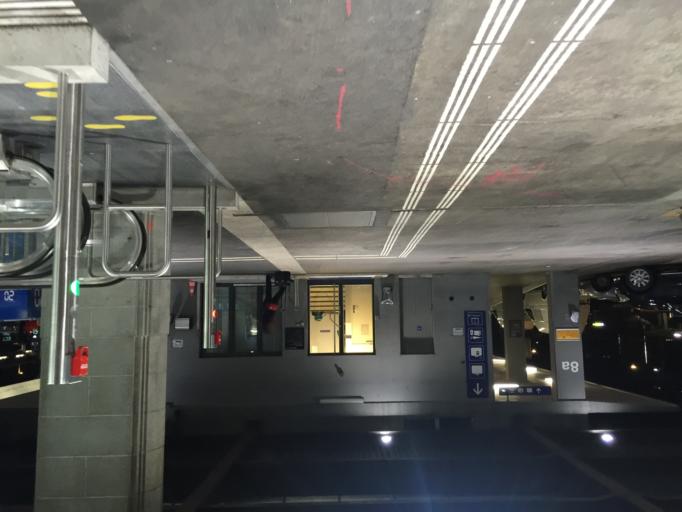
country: CH
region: Saint Gallen
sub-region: Wahlkreis St. Gallen
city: Sankt Gallen
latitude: 47.4226
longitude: 9.3688
